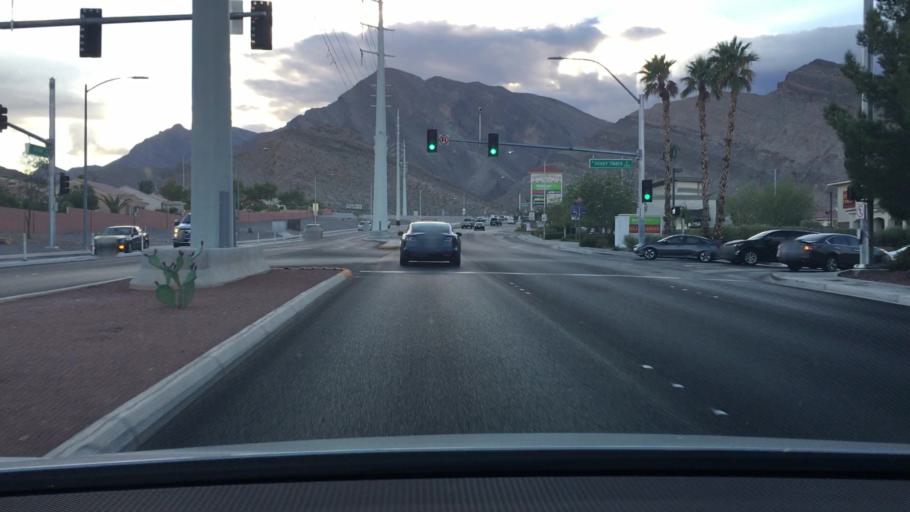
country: US
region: Nevada
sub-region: Clark County
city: Summerlin South
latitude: 36.2184
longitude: -115.3234
